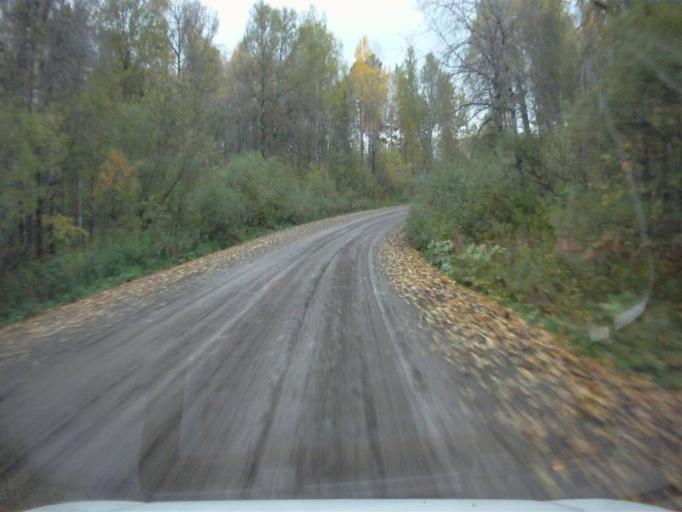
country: RU
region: Chelyabinsk
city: Nyazepetrovsk
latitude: 56.1151
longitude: 59.3680
